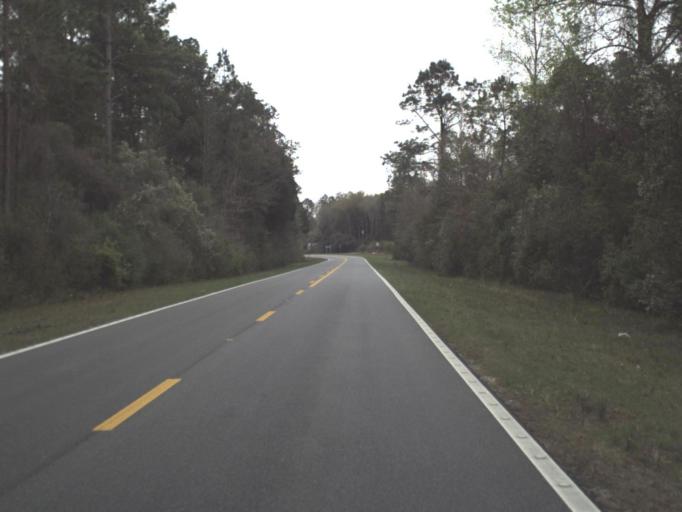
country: US
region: Florida
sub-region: Gulf County
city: Wewahitchka
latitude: 30.0317
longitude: -84.9836
